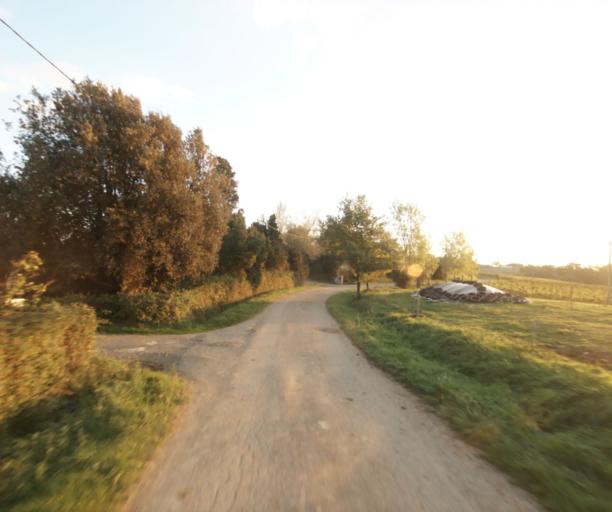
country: FR
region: Midi-Pyrenees
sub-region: Departement du Gers
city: Vic-Fezensac
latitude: 43.7726
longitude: 0.1991
